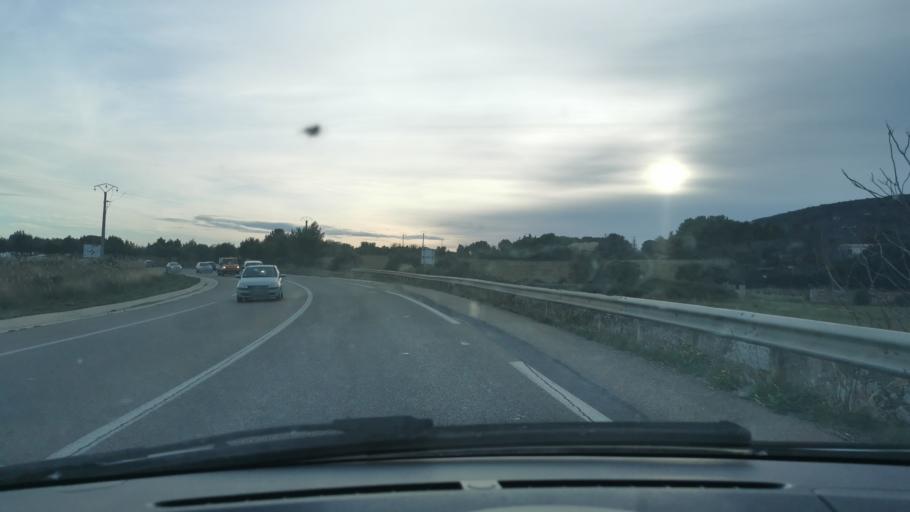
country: FR
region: Languedoc-Roussillon
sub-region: Departement de l'Herault
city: Frontignan
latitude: 43.4691
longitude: 3.7664
